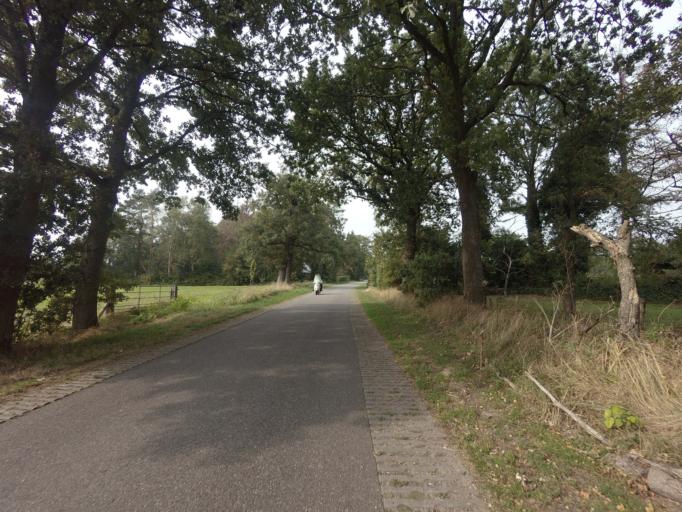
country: NL
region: Drenthe
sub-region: Gemeente Tynaarlo
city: Vries
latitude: 53.1220
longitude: 6.5688
